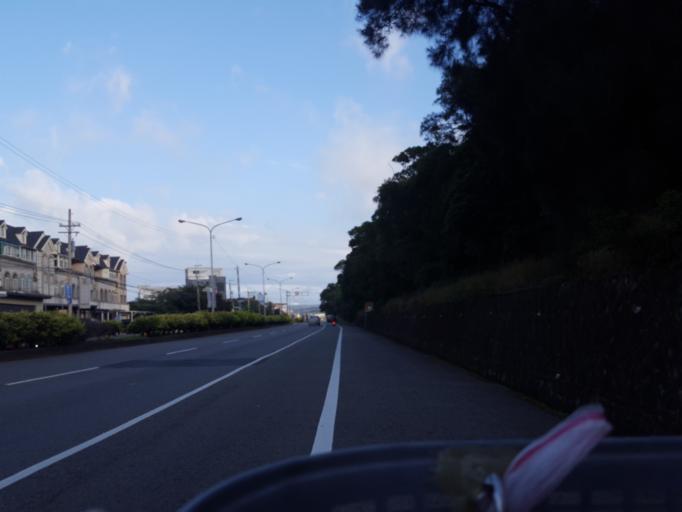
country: TW
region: Taiwan
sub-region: Hsinchu
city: Zhubei
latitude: 24.8852
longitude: 121.0230
